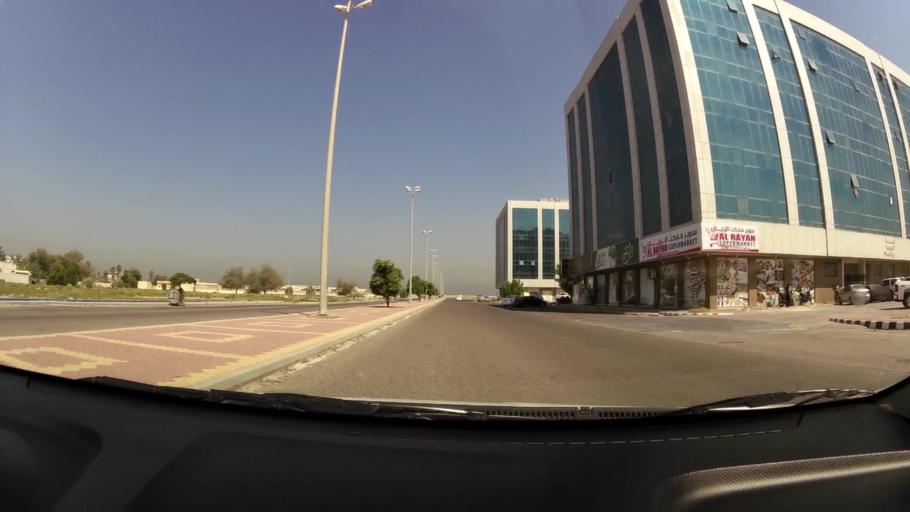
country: AE
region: Umm al Qaywayn
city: Umm al Qaywayn
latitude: 25.5767
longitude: 55.5575
